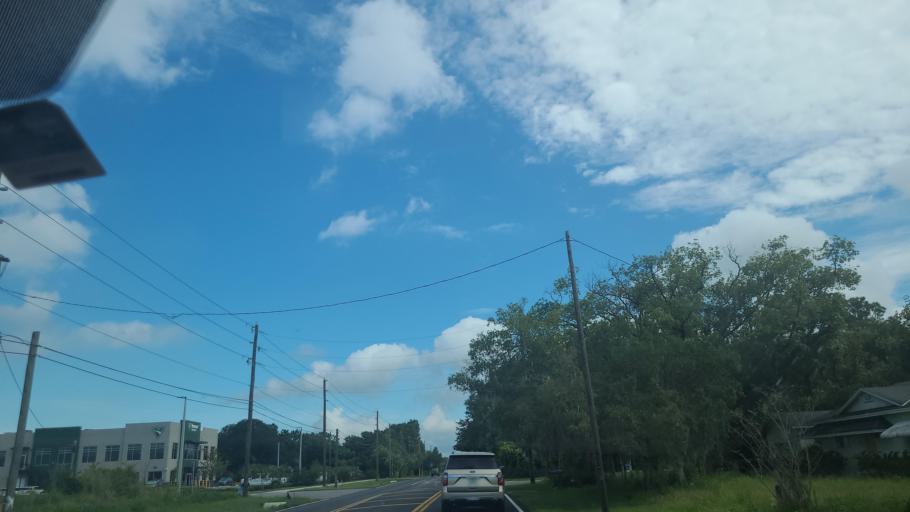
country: US
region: Florida
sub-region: Orange County
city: Ocoee
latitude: 28.5755
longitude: -81.5507
